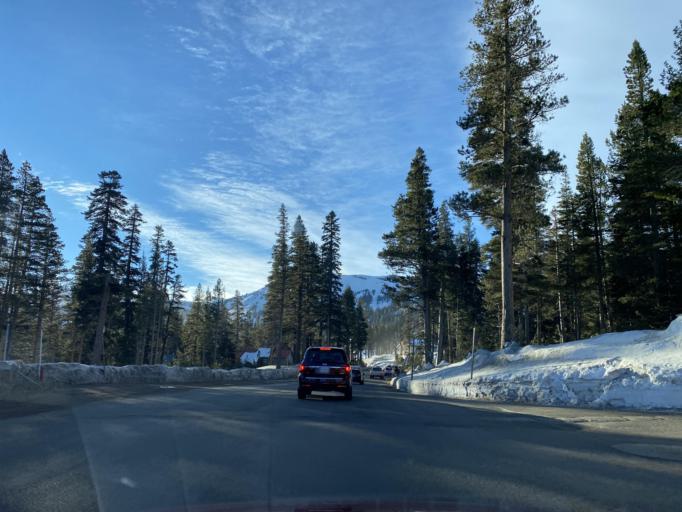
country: US
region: California
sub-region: El Dorado County
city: South Lake Tahoe
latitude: 38.6934
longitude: -120.0753
